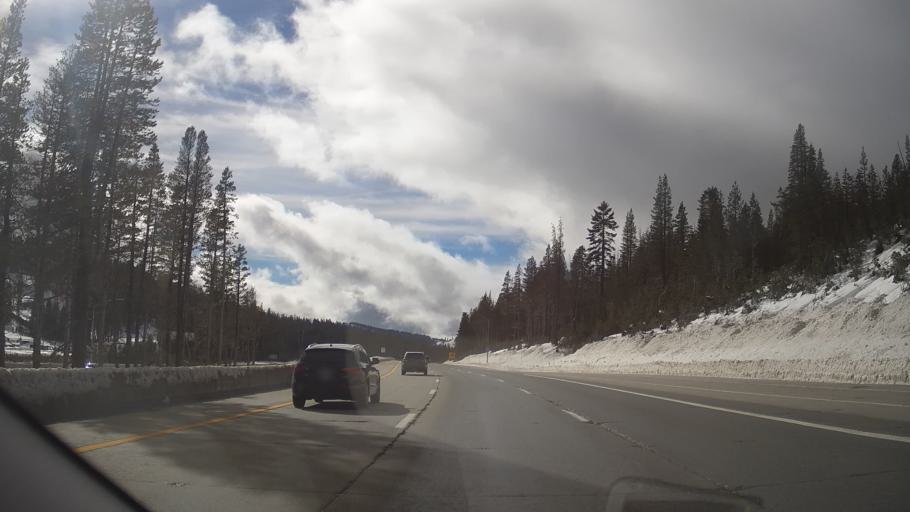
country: US
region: California
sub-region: Nevada County
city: Truckee
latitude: 39.3384
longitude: -120.3516
